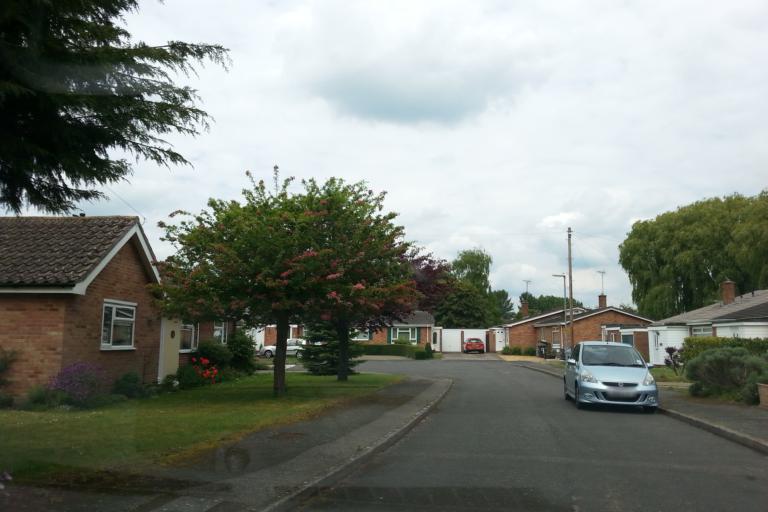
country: GB
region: England
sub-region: Cambridgeshire
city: Girton
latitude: 52.2788
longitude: 0.0500
